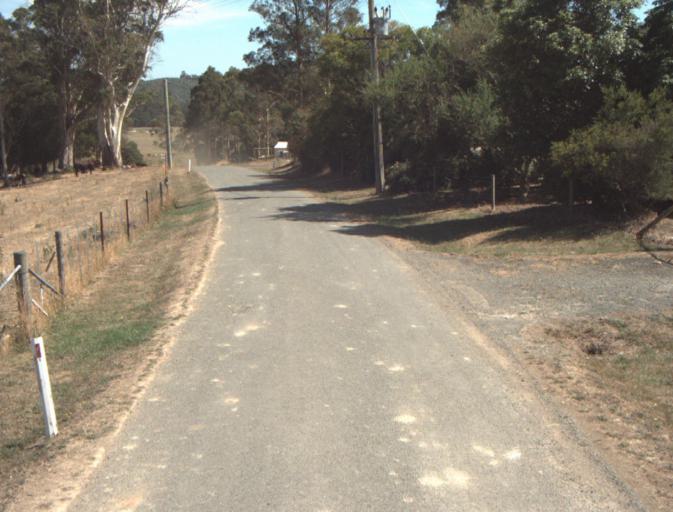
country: AU
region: Tasmania
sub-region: Launceston
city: Mayfield
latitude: -41.2342
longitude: 147.2555
